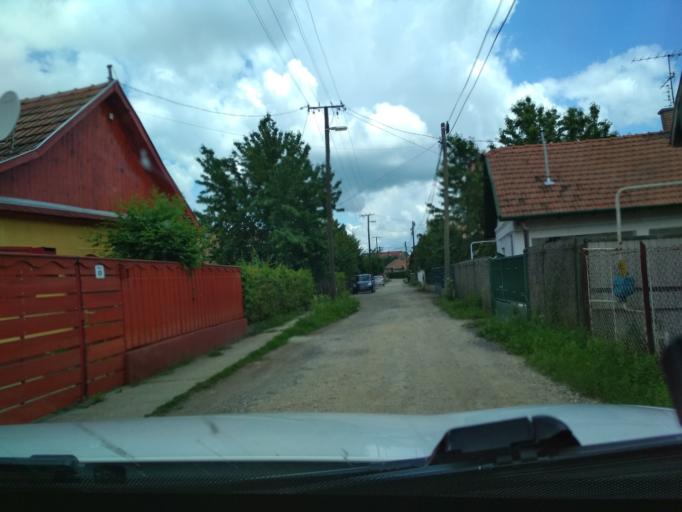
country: HU
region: Jasz-Nagykun-Szolnok
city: Tiszafured
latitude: 47.6049
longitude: 20.7717
